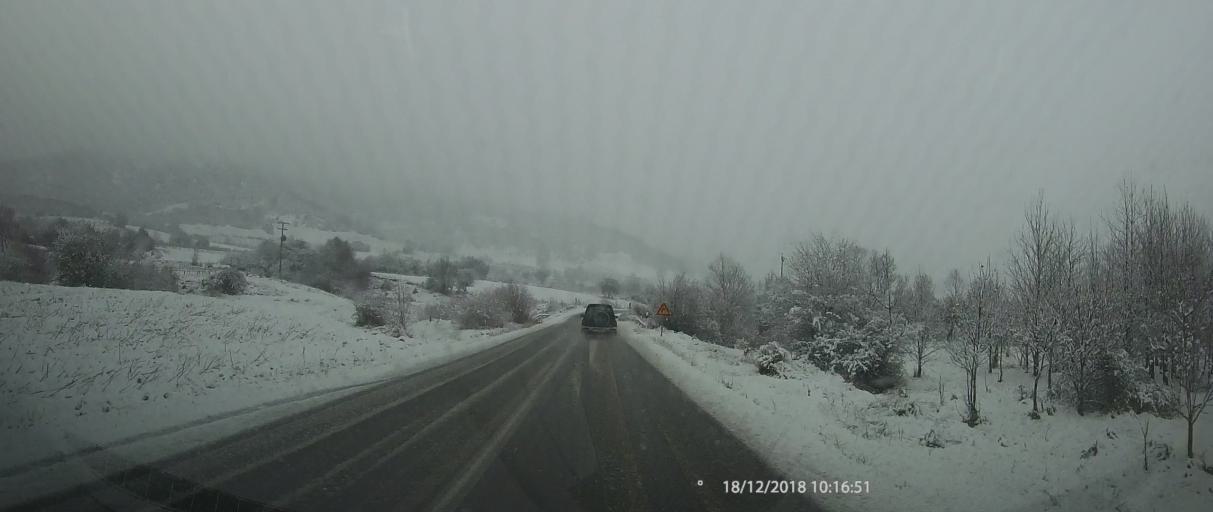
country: GR
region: Thessaly
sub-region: Nomos Larisis
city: Livadi
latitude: 40.1195
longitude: 22.2107
